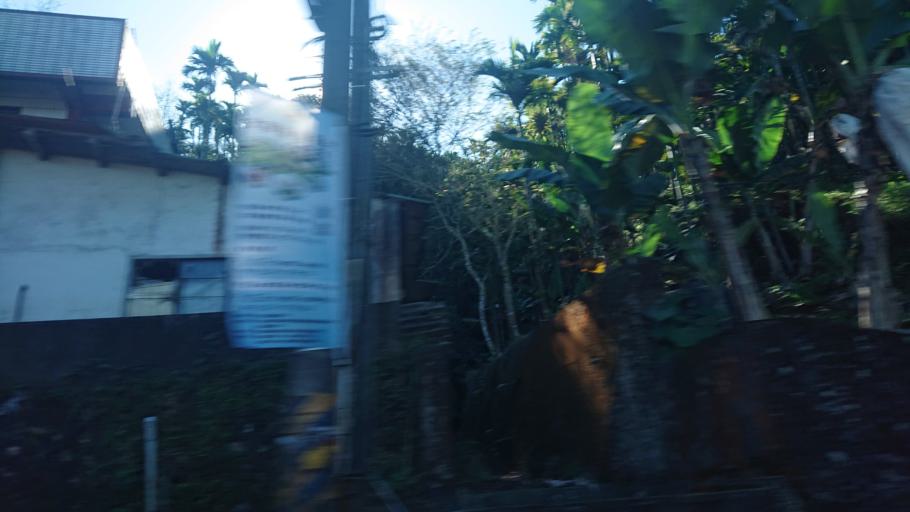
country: TW
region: Taiwan
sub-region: Chiayi
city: Jiayi Shi
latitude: 23.5189
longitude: 120.6288
